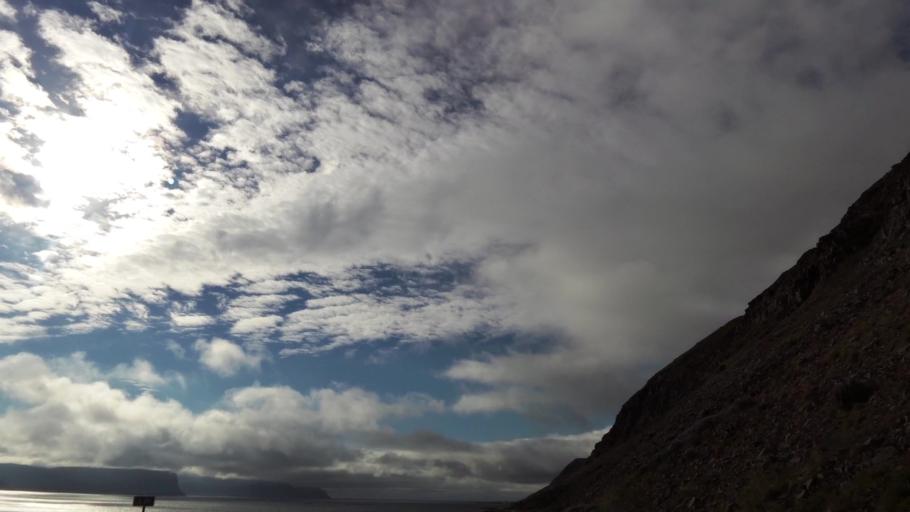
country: IS
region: West
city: Olafsvik
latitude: 65.5685
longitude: -23.9268
